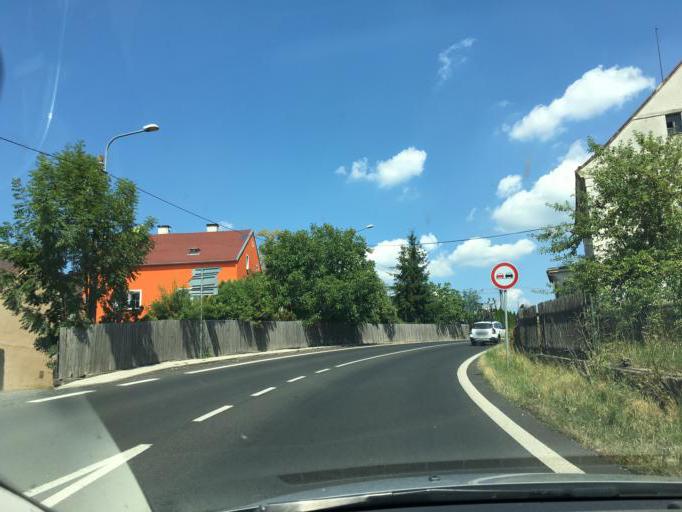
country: CZ
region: Ustecky
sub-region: Okres Decin
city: Decin
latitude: 50.7907
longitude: 14.2531
